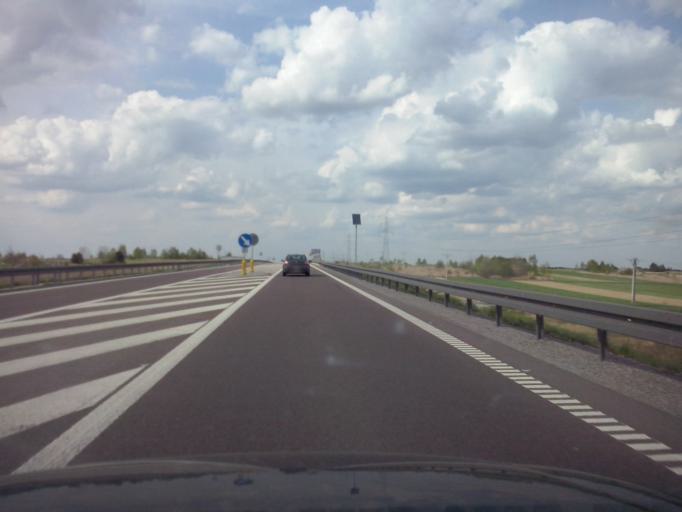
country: PL
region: Subcarpathian Voivodeship
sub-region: Powiat rzeszowski
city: Wolka Podlesna
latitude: 50.1380
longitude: 22.0794
